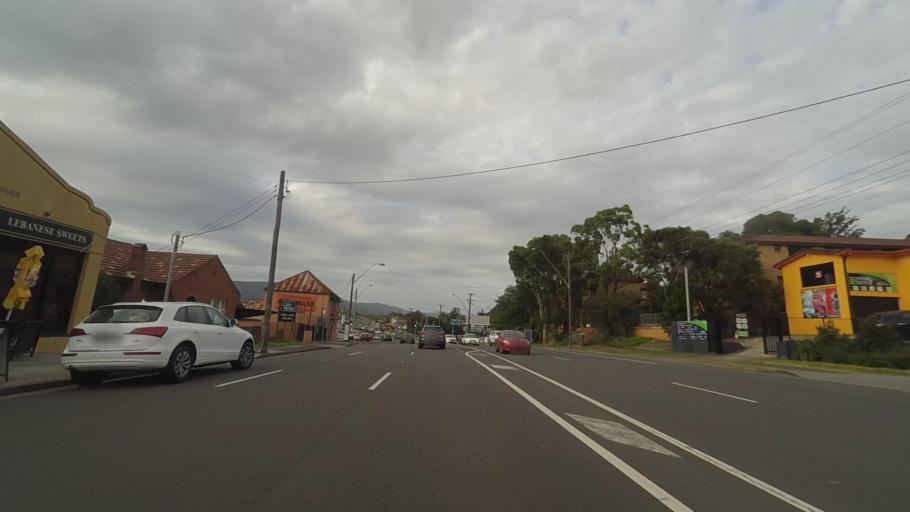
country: AU
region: New South Wales
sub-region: Wollongong
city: Gwynneville
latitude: -34.4149
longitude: 150.8929
